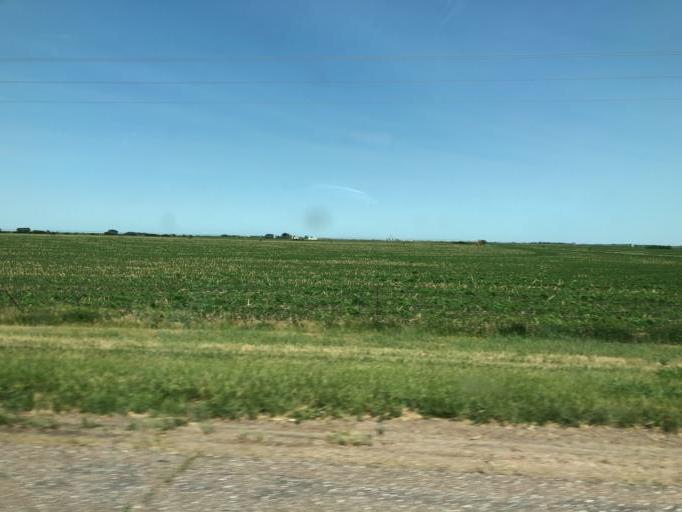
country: US
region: Nebraska
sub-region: Fillmore County
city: Geneva
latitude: 40.4669
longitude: -97.5959
